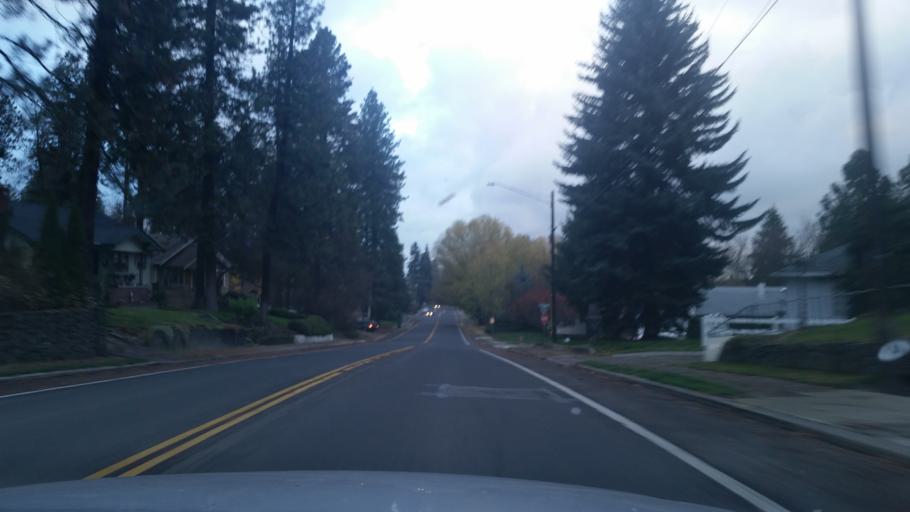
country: US
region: Washington
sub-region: Spokane County
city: Spokane
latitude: 47.6413
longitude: -117.3944
